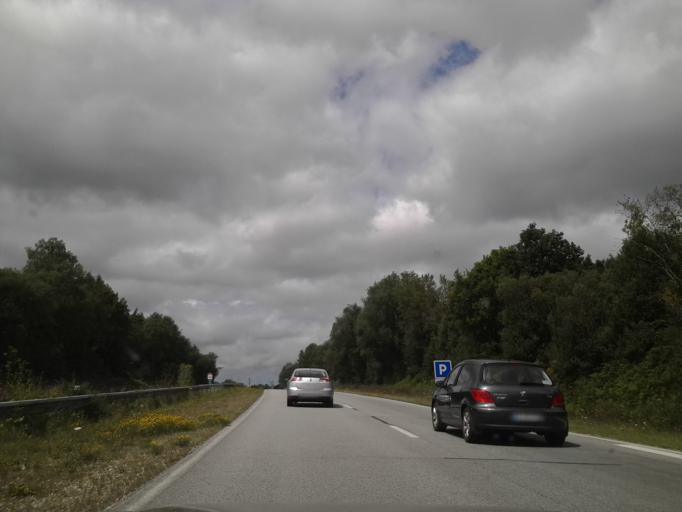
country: FR
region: Lower Normandy
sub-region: Departement de la Manche
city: Brix
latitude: 49.5659
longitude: -1.5704
